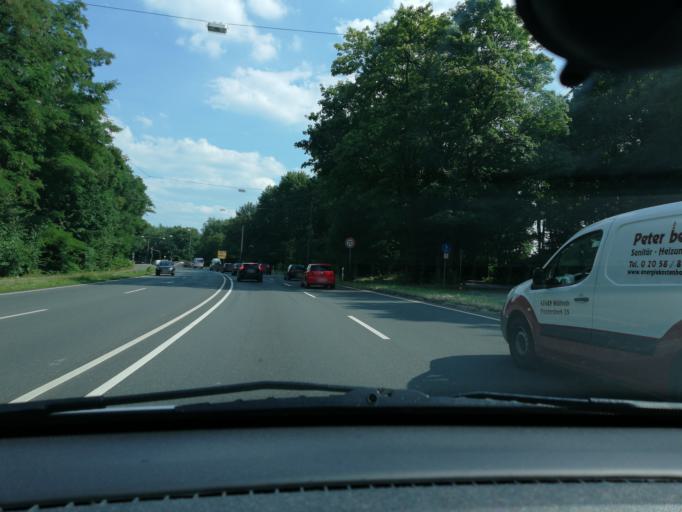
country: DE
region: North Rhine-Westphalia
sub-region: Regierungsbezirk Dusseldorf
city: Wuppertal
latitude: 51.2392
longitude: 7.1935
